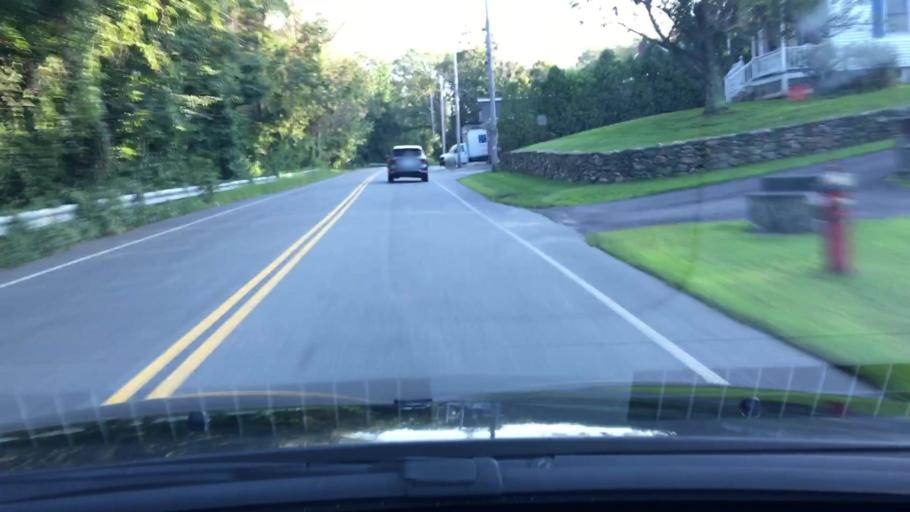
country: US
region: Massachusetts
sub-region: Worcester County
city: West Boylston
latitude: 42.3470
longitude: -71.7836
